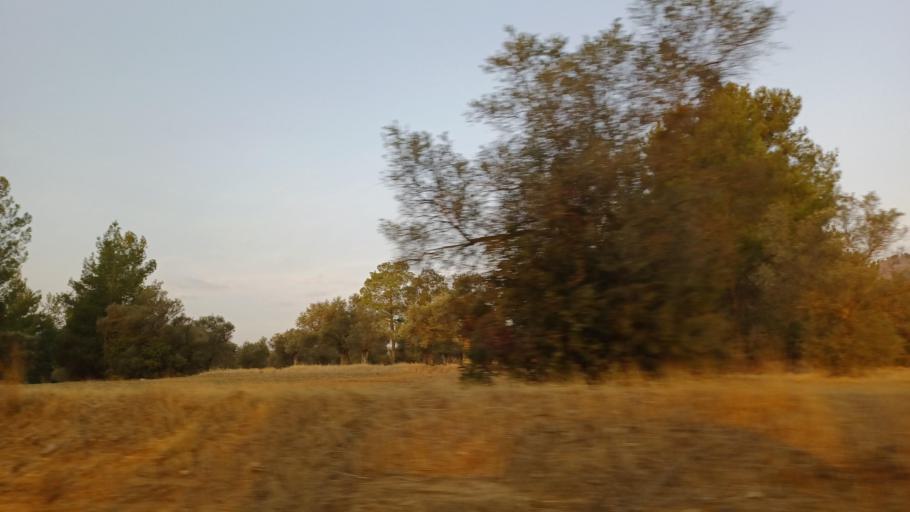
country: CY
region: Larnaka
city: Kornos
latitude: 34.9231
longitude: 33.3899
